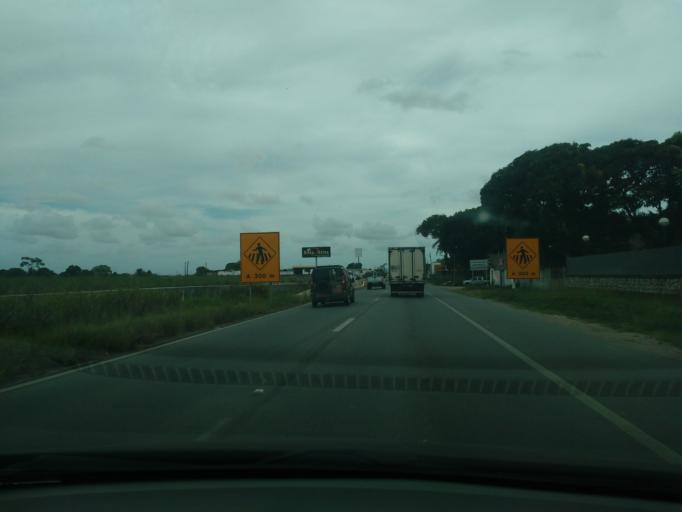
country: BR
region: Alagoas
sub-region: Rio Largo
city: Rio Largo
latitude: -9.5035
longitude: -35.8102
